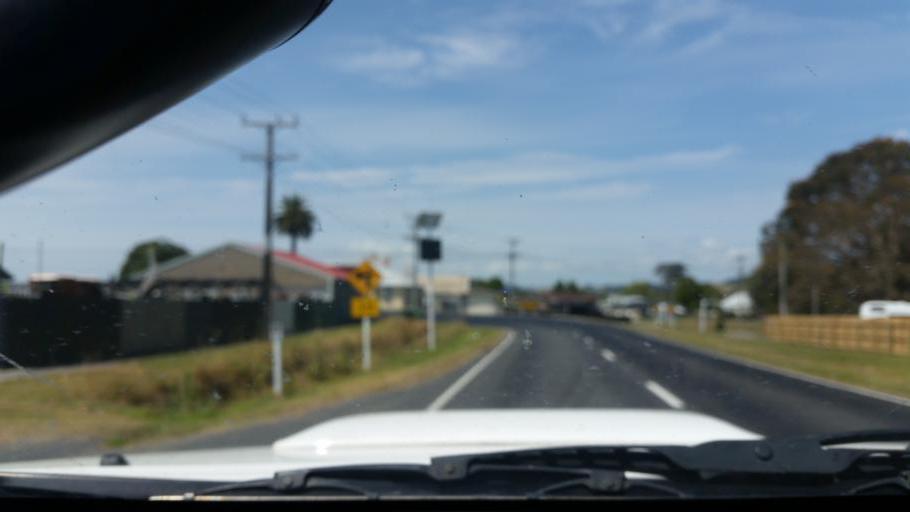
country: NZ
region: Northland
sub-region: Kaipara District
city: Dargaville
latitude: -36.0314
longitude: 173.9227
